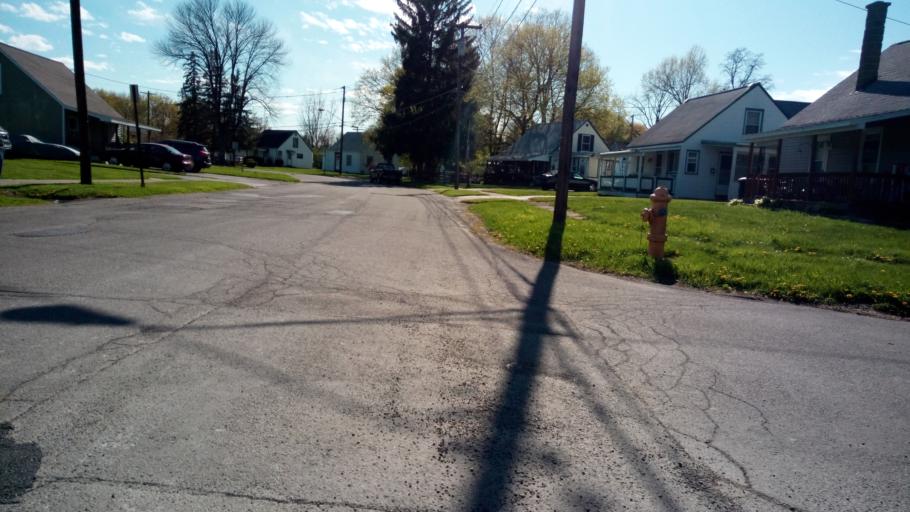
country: US
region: New York
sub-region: Chemung County
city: Southport
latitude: 42.0655
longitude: -76.7998
